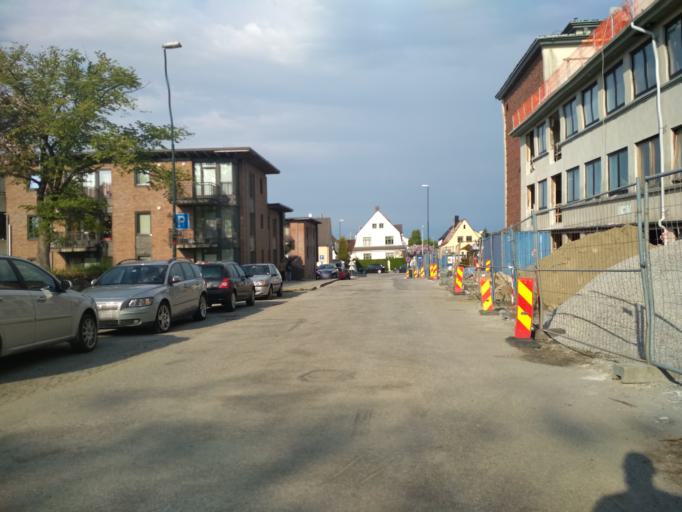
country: NO
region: Rogaland
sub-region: Stavanger
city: Stavanger
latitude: 58.9677
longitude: 5.7206
